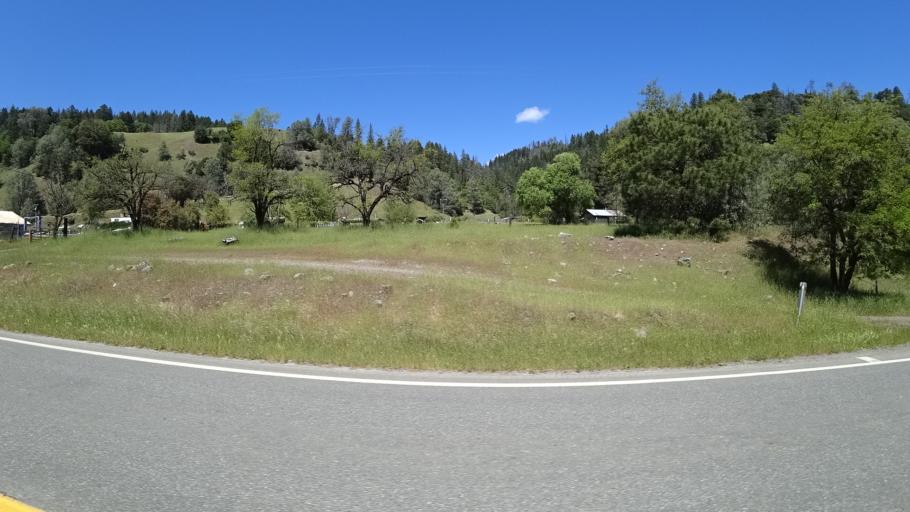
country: US
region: California
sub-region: Trinity County
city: Hayfork
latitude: 40.7404
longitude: -123.2538
